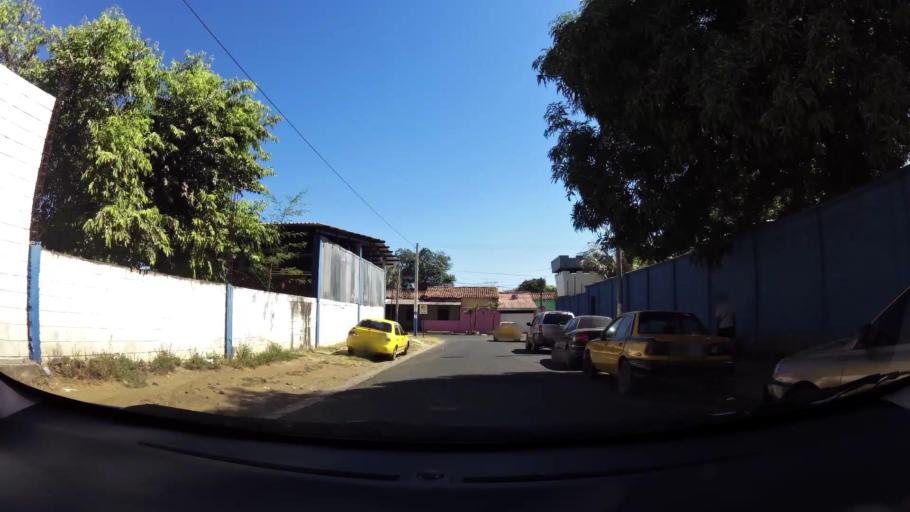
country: SV
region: San Miguel
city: San Miguel
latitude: 13.4771
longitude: -88.1708
